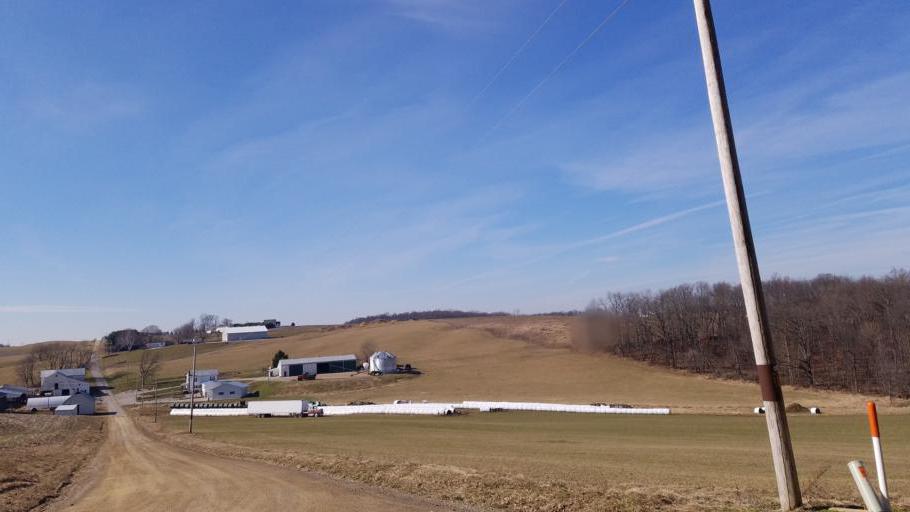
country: US
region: Ohio
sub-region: Knox County
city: Mount Vernon
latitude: 40.4876
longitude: -82.4320
